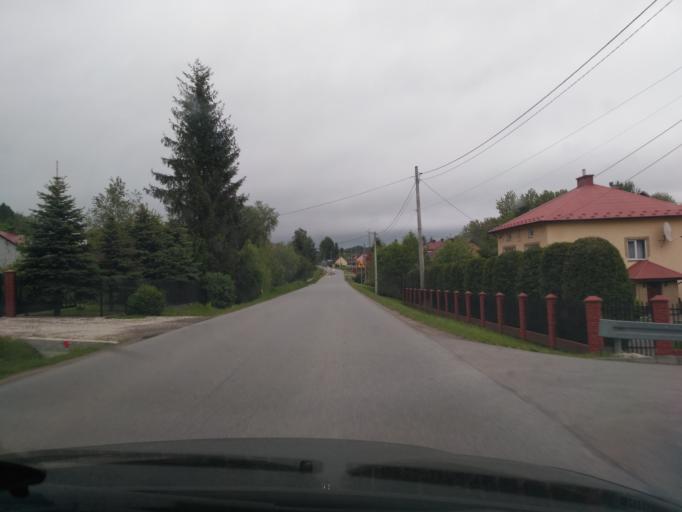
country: PL
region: Subcarpathian Voivodeship
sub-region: Powiat debicki
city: Jodlowa
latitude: 49.8815
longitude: 21.3195
